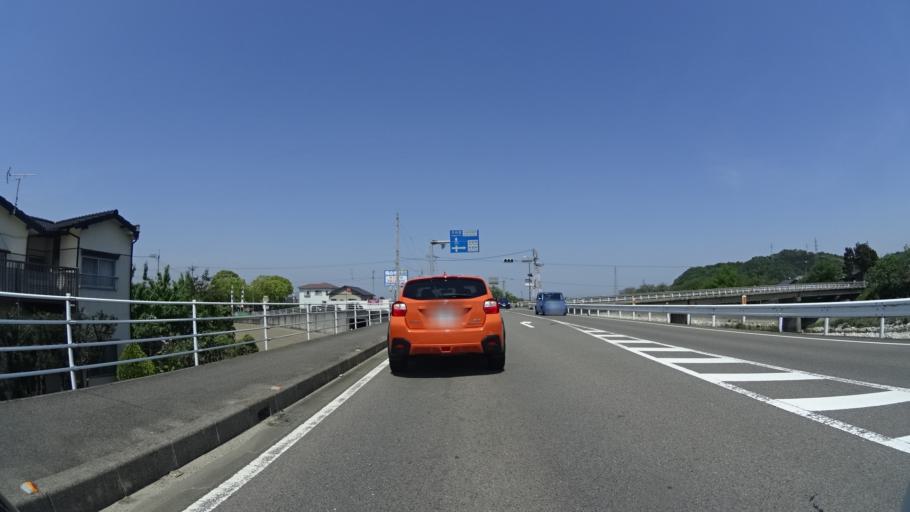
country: JP
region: Ehime
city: Hojo
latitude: 34.0322
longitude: 132.9681
